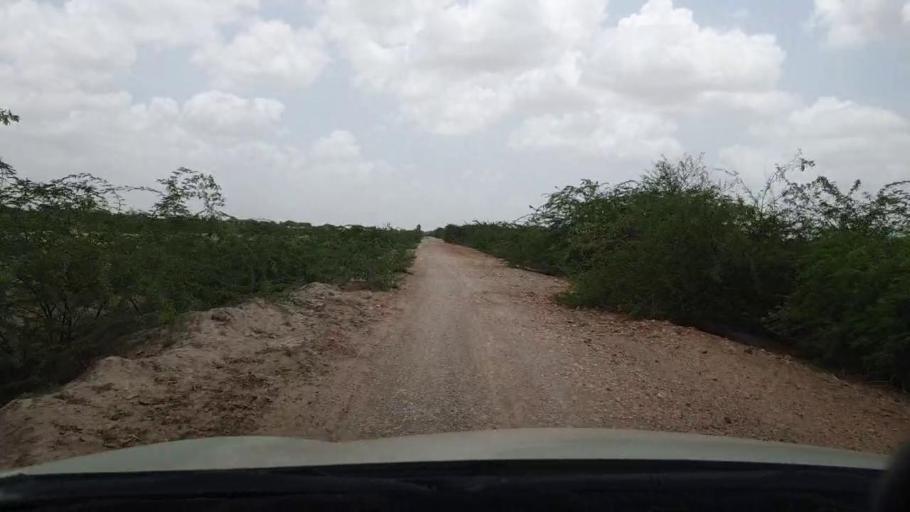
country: PK
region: Sindh
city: Kadhan
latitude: 24.3834
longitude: 68.9314
